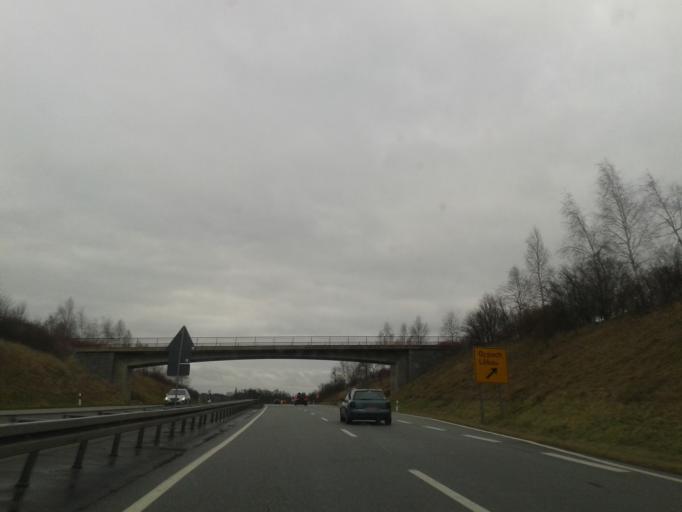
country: DE
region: Saxony
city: Grossschweidnitz
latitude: 51.0925
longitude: 14.6407
